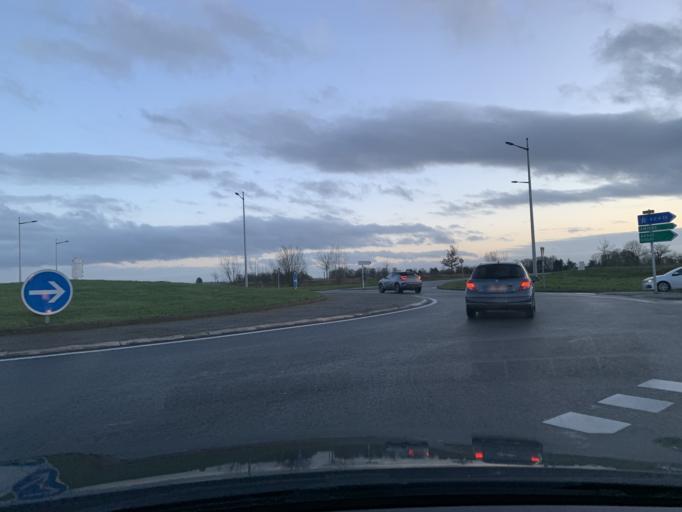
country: FR
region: Nord-Pas-de-Calais
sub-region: Departement du Nord
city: Cambrai
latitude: 50.1522
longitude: 3.2638
